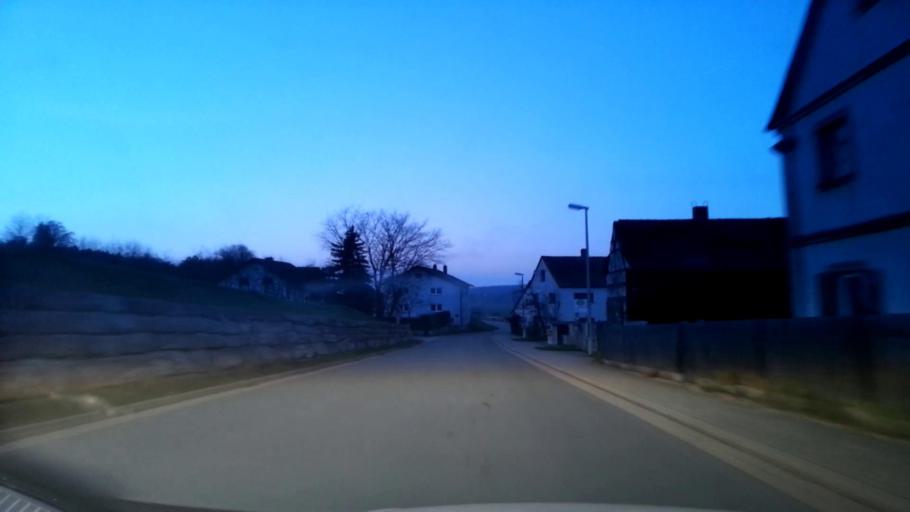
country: DE
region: Bavaria
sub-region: Upper Franconia
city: Pettstadt
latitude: 49.8430
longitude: 10.9153
